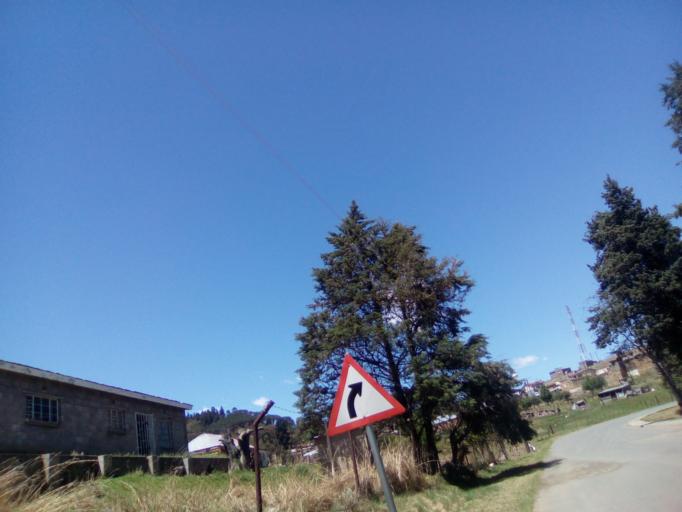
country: LS
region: Qacha's Nek
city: Qacha's Nek
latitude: -30.1208
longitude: 28.6919
